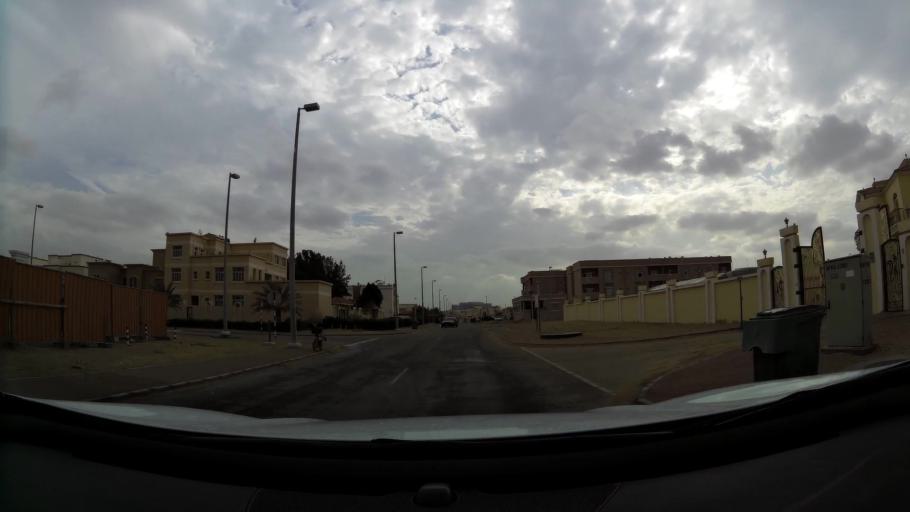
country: AE
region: Abu Dhabi
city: Abu Dhabi
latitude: 24.3421
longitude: 54.6286
